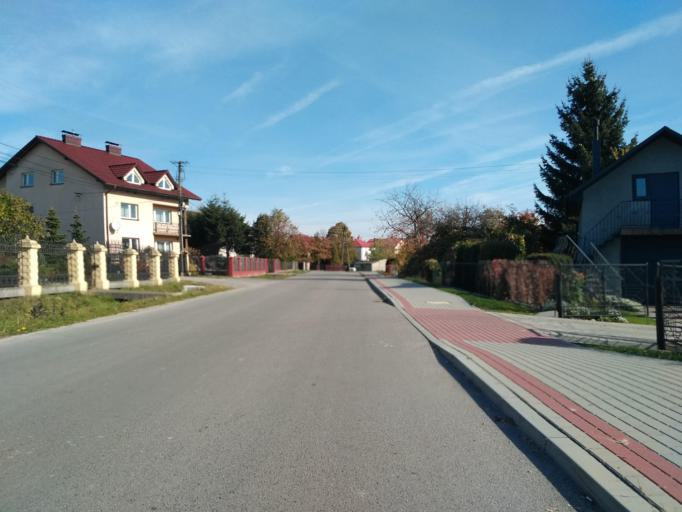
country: PL
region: Subcarpathian Voivodeship
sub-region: Powiat ropczycko-sedziszowski
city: Iwierzyce
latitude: 50.0721
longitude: 21.7816
